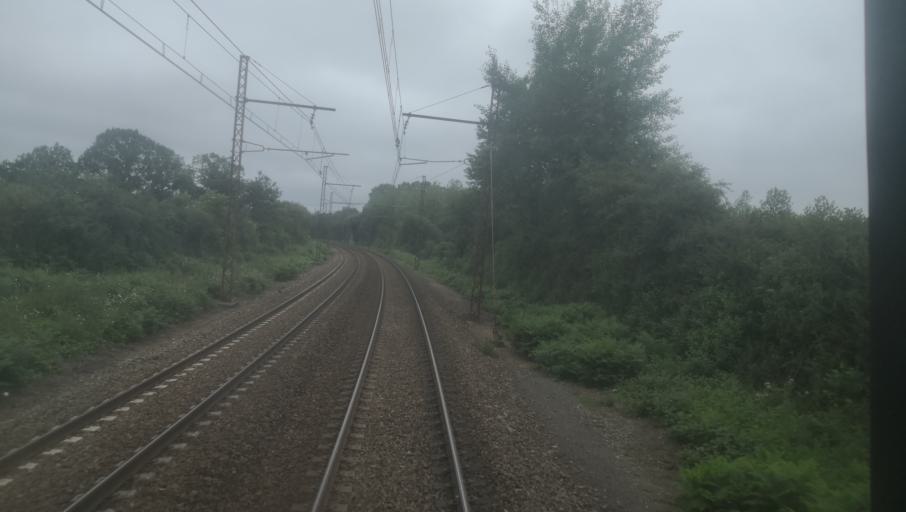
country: FR
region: Limousin
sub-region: Departement de la Creuse
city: La Souterraine
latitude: 46.2304
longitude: 1.4967
